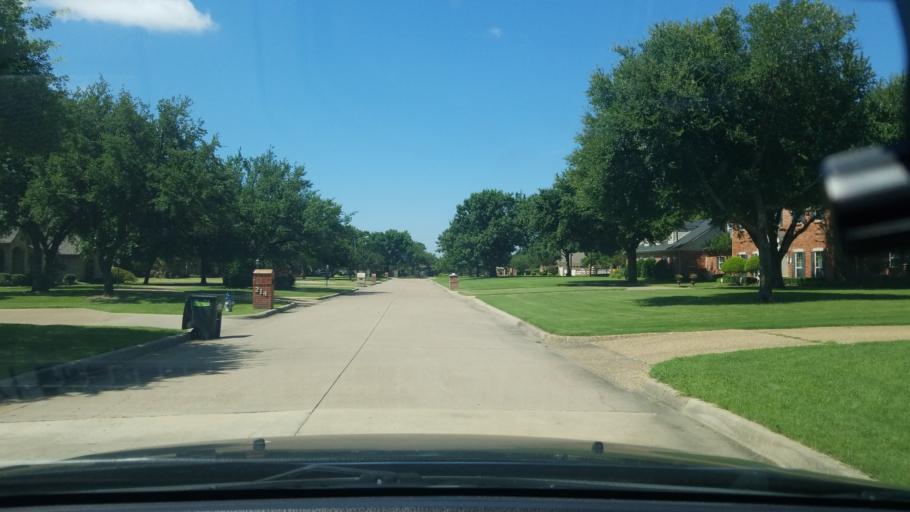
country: US
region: Texas
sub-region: Dallas County
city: Sunnyvale
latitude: 32.8014
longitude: -96.5910
